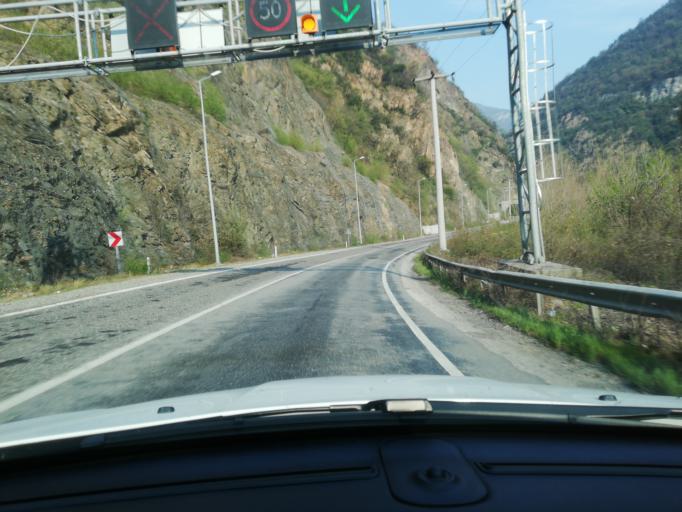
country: TR
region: Karabuk
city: Yenice
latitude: 41.1589
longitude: 32.4604
